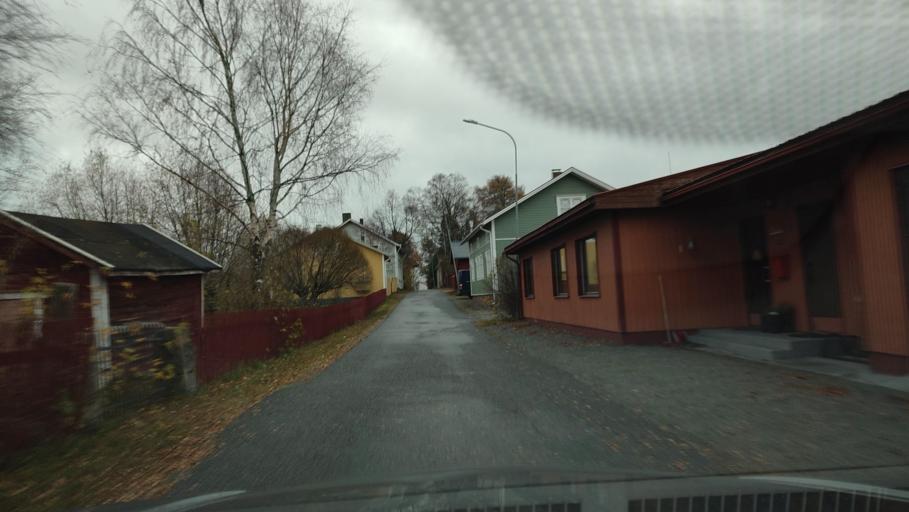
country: FI
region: Ostrobothnia
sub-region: Sydosterbotten
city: Kristinestad
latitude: 62.2800
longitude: 21.3772
